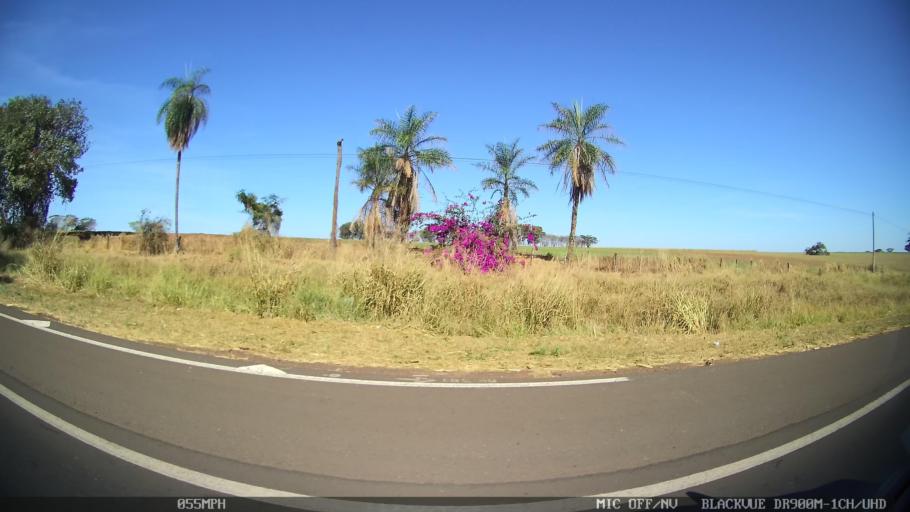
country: BR
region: Sao Paulo
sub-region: Olimpia
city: Olimpia
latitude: -20.6732
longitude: -48.8799
